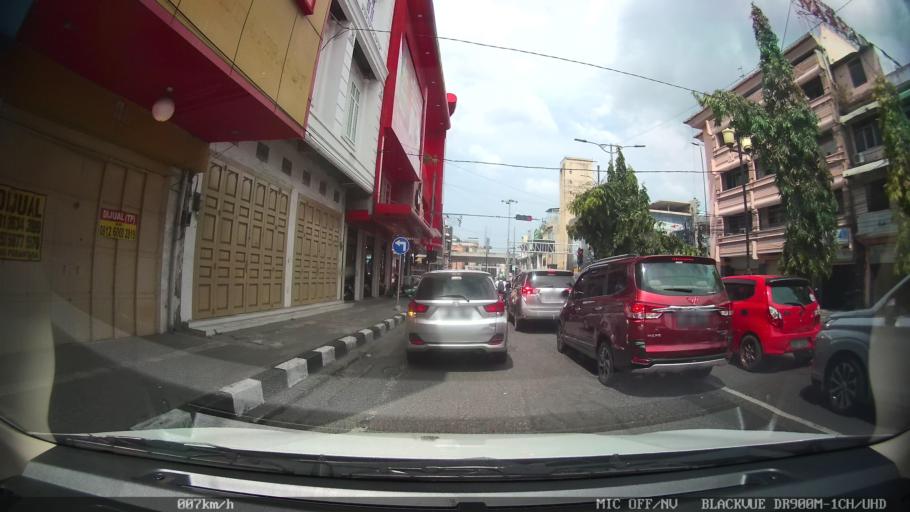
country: ID
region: North Sumatra
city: Medan
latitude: 3.5811
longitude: 98.6822
